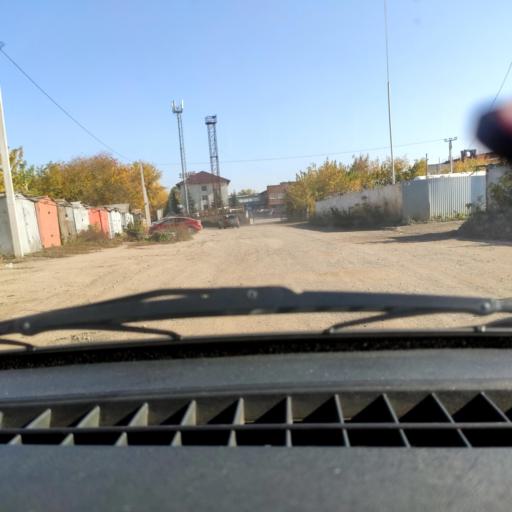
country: RU
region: Bashkortostan
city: Ufa
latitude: 54.7731
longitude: 56.1287
